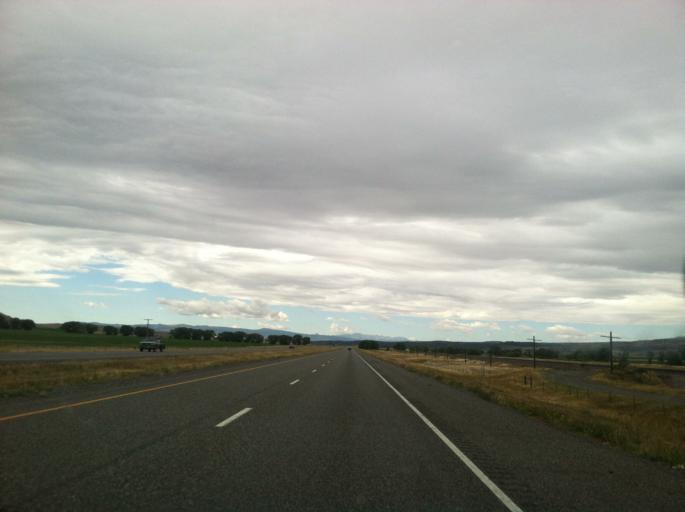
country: US
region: Montana
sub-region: Park County
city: Livingston
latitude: 45.6988
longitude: -110.3195
